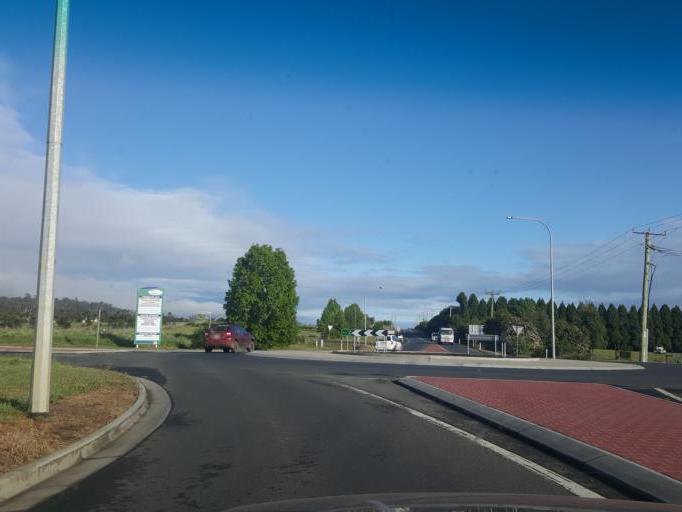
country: AU
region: Tasmania
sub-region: Northern Midlands
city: Perth
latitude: -41.5367
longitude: 147.1961
